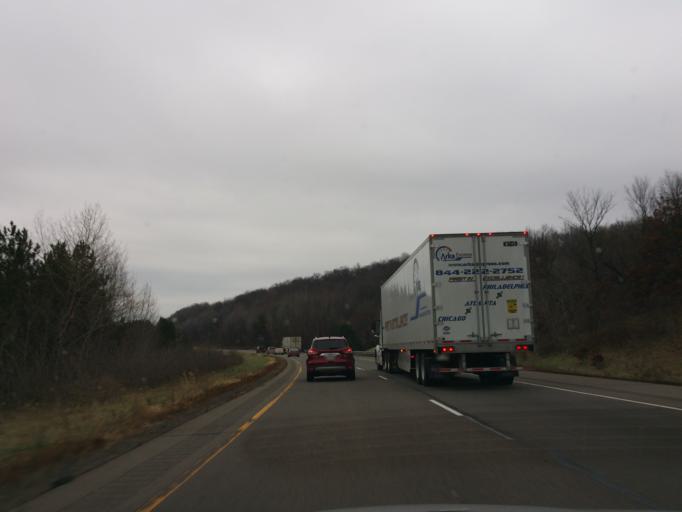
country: US
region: Wisconsin
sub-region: Trempealeau County
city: Osseo
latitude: 44.4441
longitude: -91.0798
